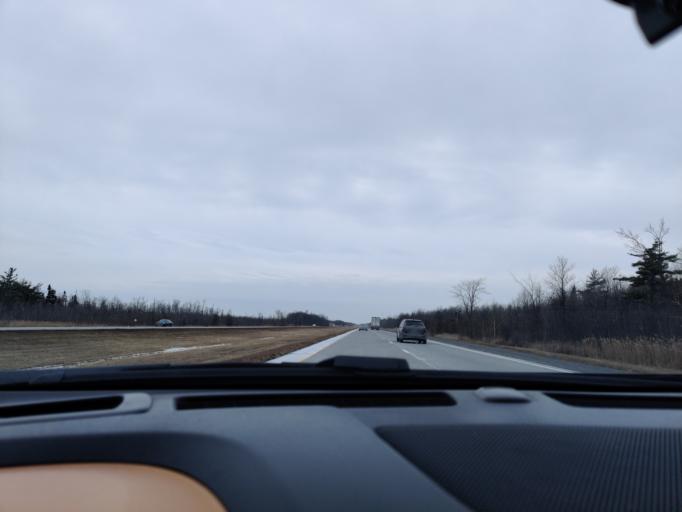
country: US
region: New York
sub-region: St. Lawrence County
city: Massena
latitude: 45.0020
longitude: -75.0212
